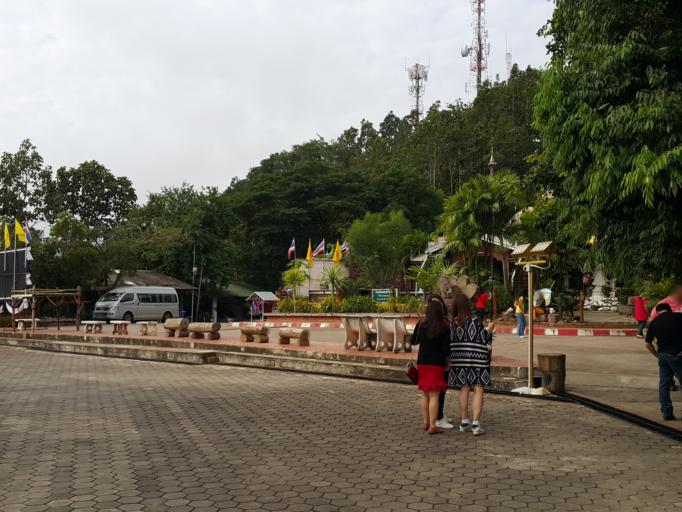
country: TH
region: Mae Hong Son
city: Mae Hong Son
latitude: 19.3002
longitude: 97.9603
